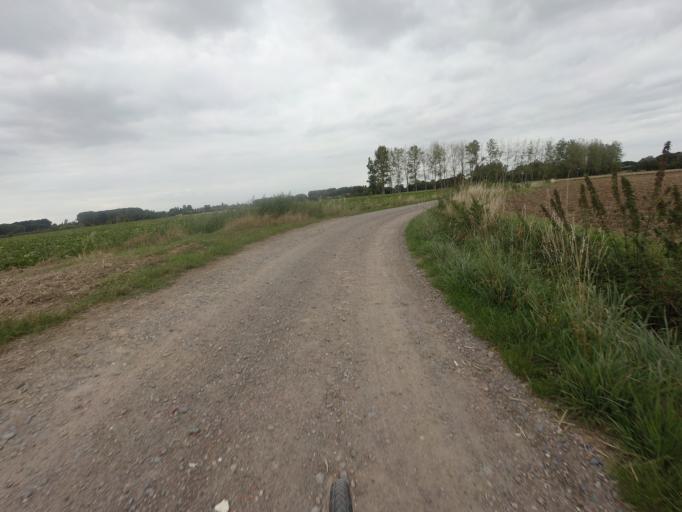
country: BE
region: Flanders
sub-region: Provincie Vlaams-Brabant
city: Herent
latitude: 50.9096
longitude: 4.6517
